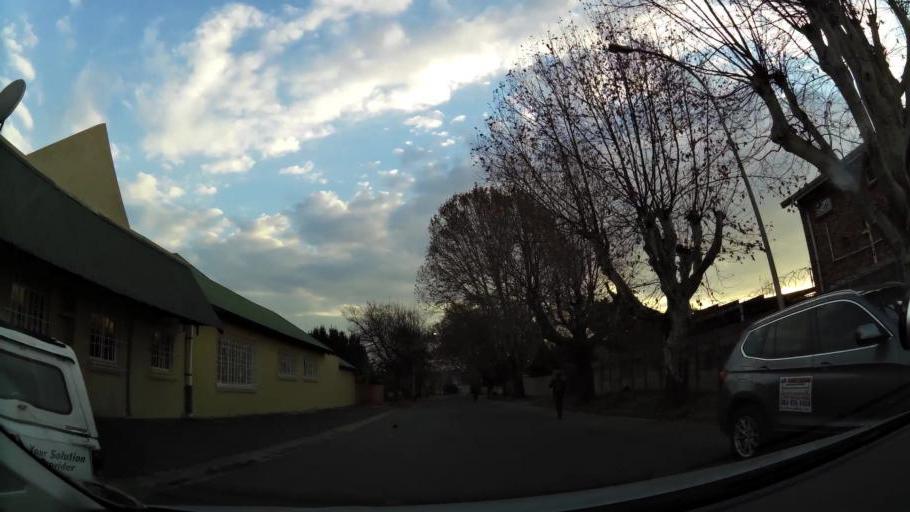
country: ZA
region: Gauteng
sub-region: Ekurhuleni Metropolitan Municipality
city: Germiston
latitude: -26.1915
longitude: 28.1608
